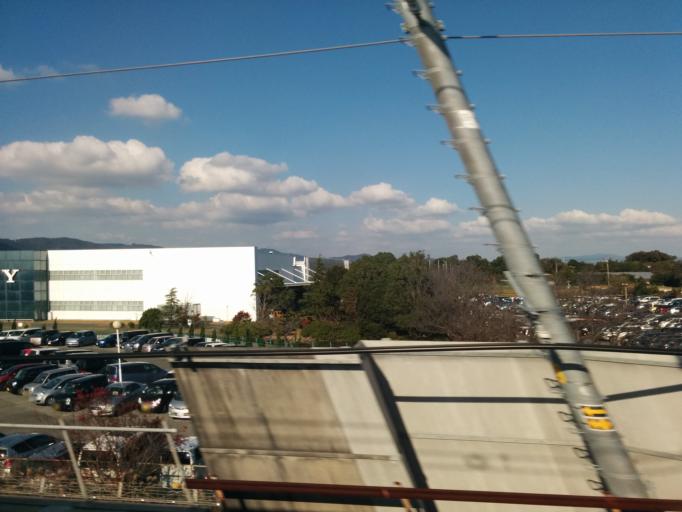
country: JP
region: Shizuoka
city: Kosai-shi
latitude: 34.7118
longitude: 137.4974
